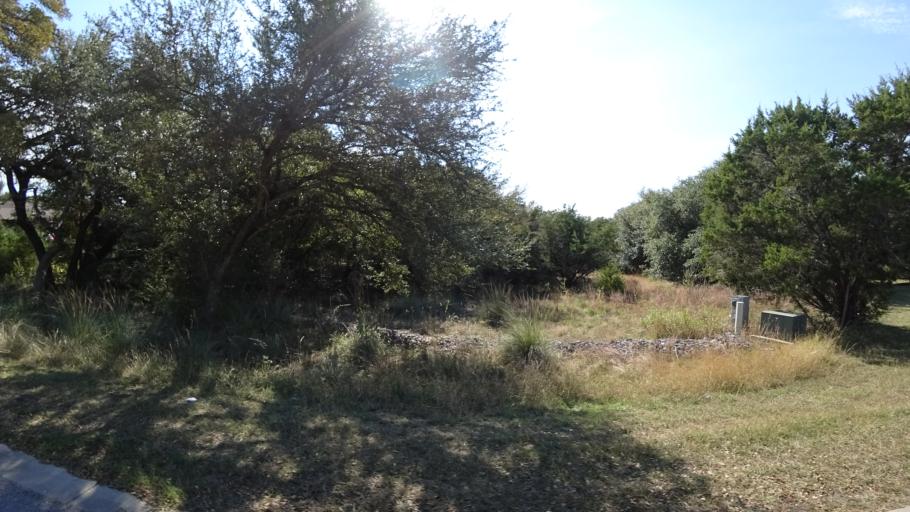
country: US
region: Texas
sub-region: Travis County
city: Barton Creek
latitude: 30.2239
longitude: -97.9135
